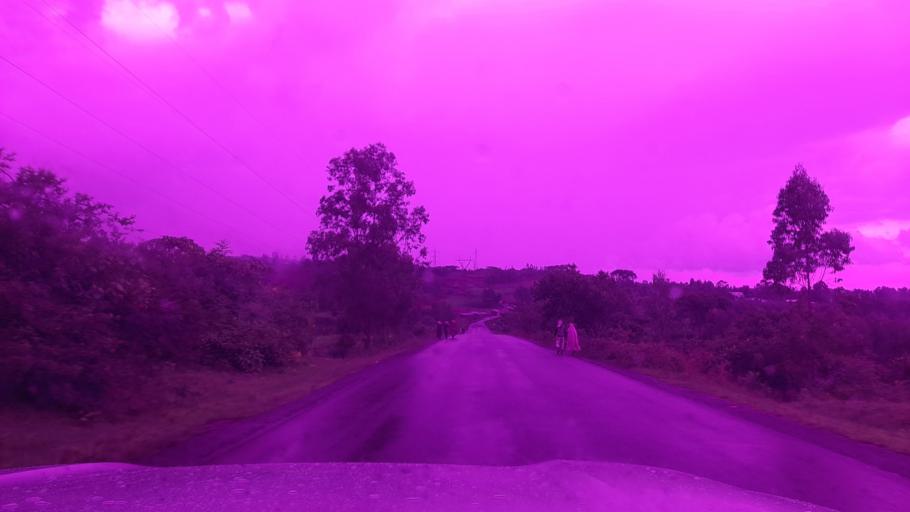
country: ET
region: Oromiya
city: Jima
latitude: 7.7131
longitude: 37.0841
